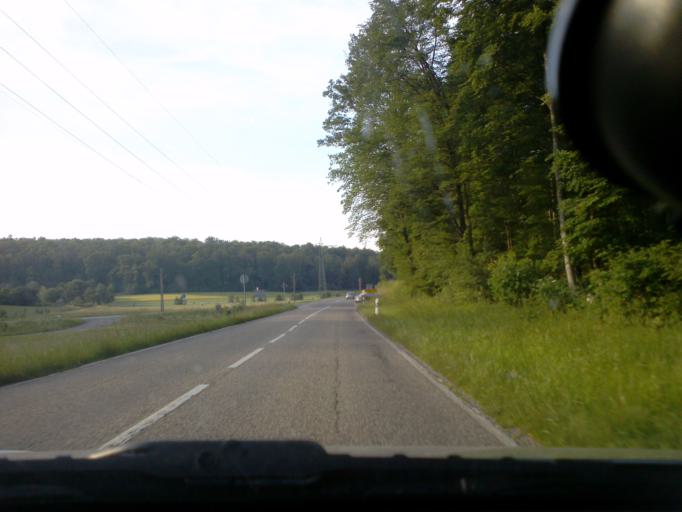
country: DE
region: Baden-Wuerttemberg
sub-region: Karlsruhe Region
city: Bretten
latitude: 49.0120
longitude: 8.6802
